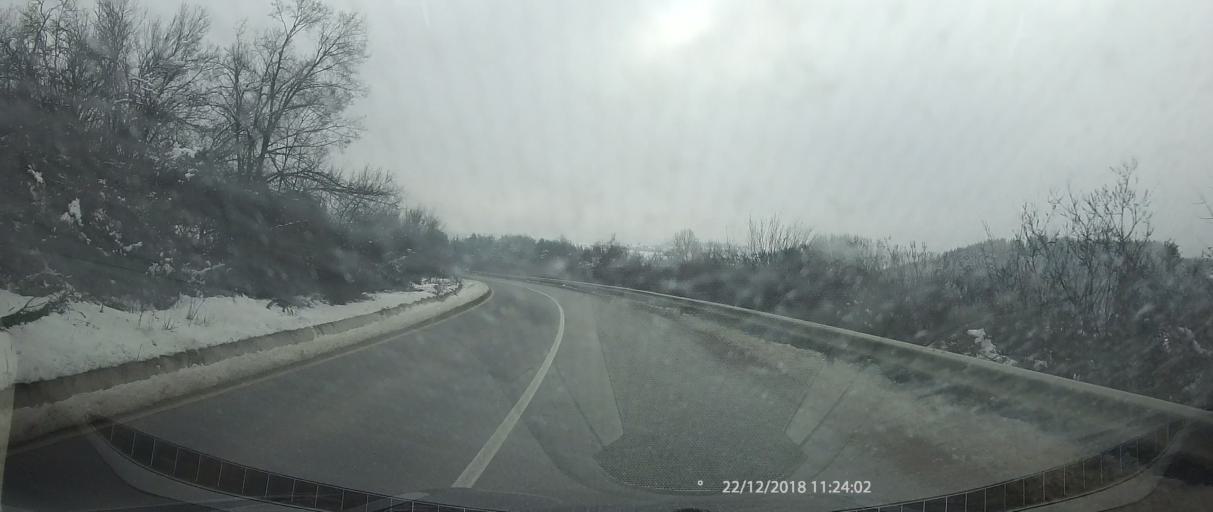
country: BG
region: Kyustendil
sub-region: Obshtina Boboshevo
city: Boboshevo
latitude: 42.2528
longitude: 22.8863
